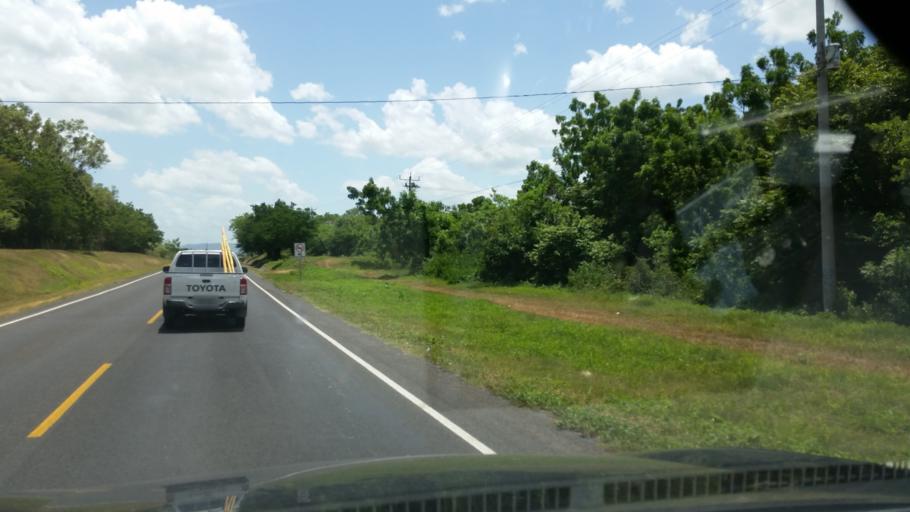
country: NI
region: Managua
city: Tipitapa
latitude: 12.3844
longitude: -86.0451
